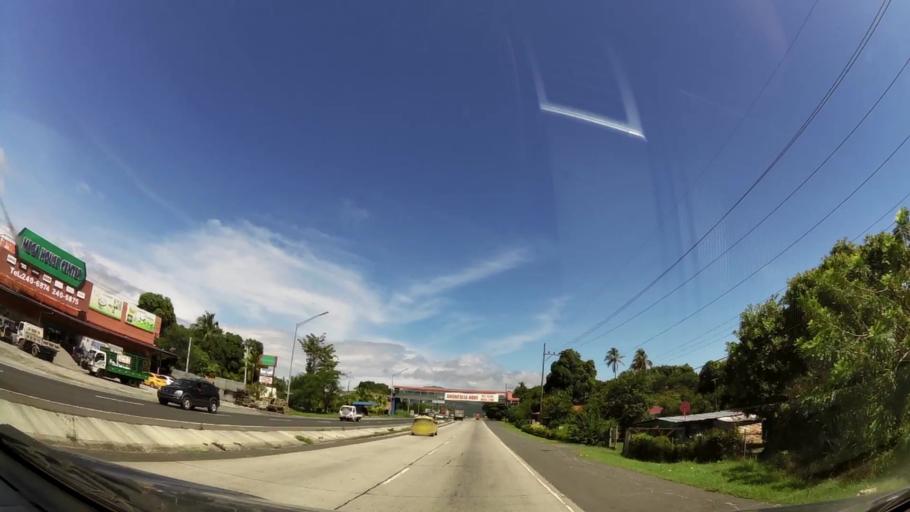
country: PA
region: Panama
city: Chame
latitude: 8.5623
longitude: -79.8960
